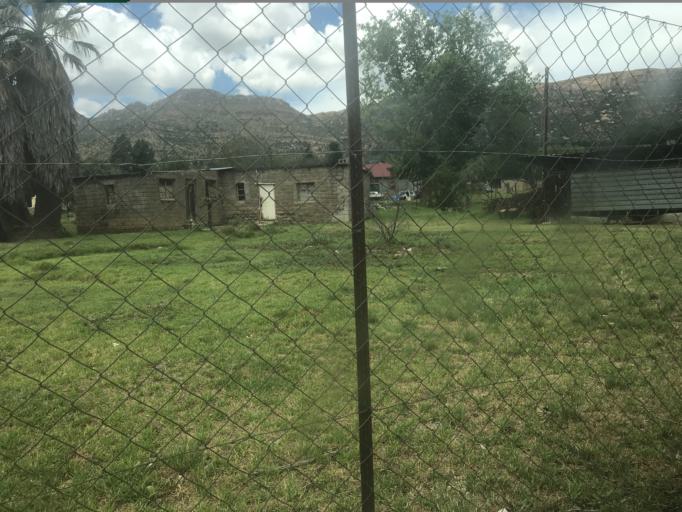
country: LS
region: Maseru
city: Nako
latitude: -29.6226
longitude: 27.5048
